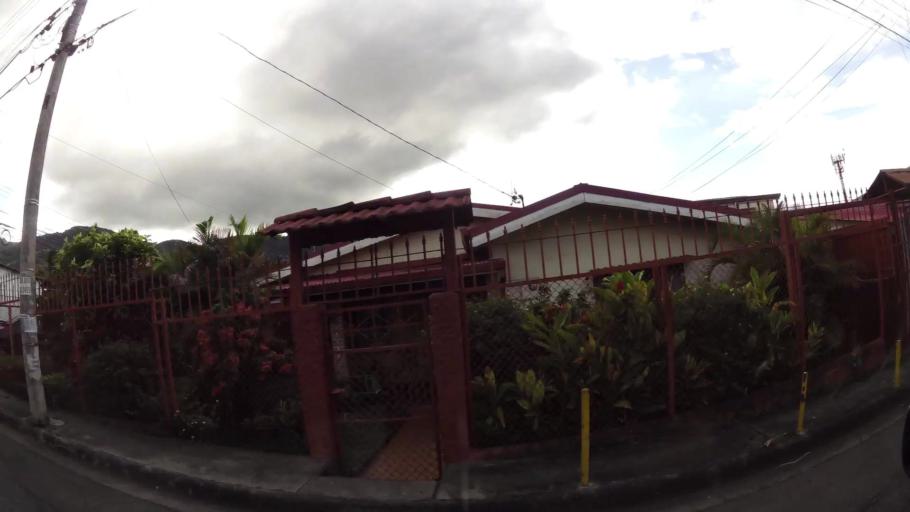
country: CR
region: San Jose
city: Escazu
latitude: 9.9171
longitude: -84.1410
